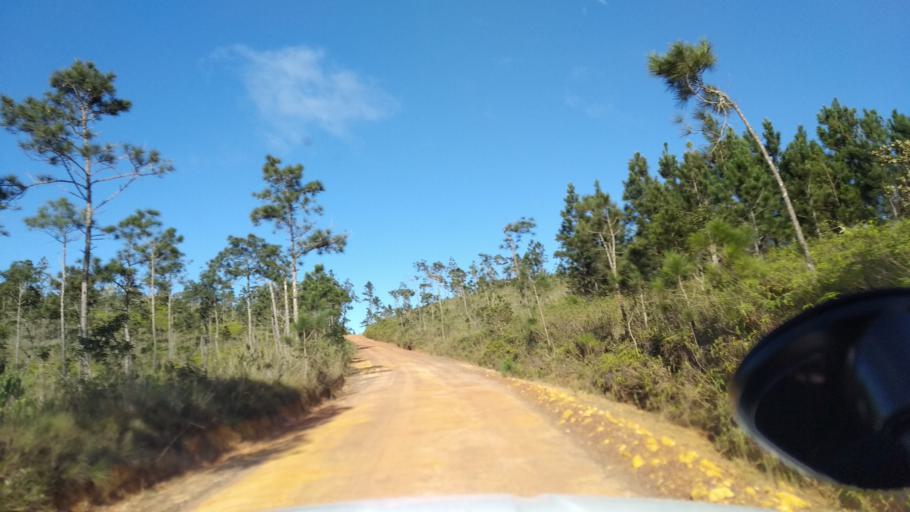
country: BZ
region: Cayo
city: Belmopan
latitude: 16.9984
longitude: -88.8457
